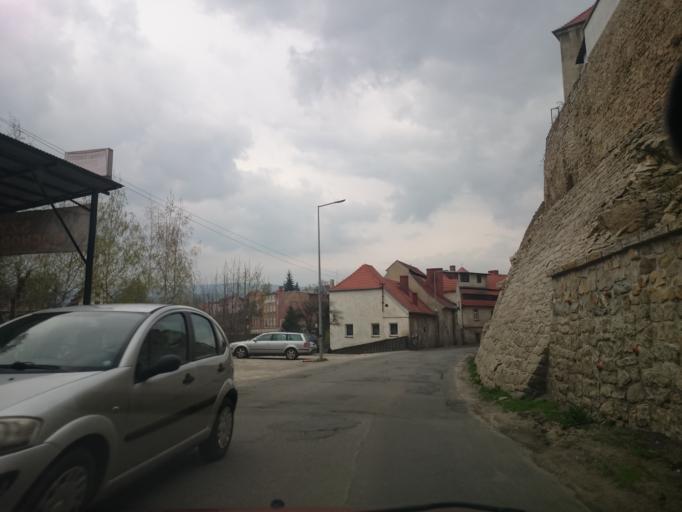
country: PL
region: Lower Silesian Voivodeship
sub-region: Powiat klodzki
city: Bystrzyca Klodzka
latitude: 50.2957
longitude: 16.6528
